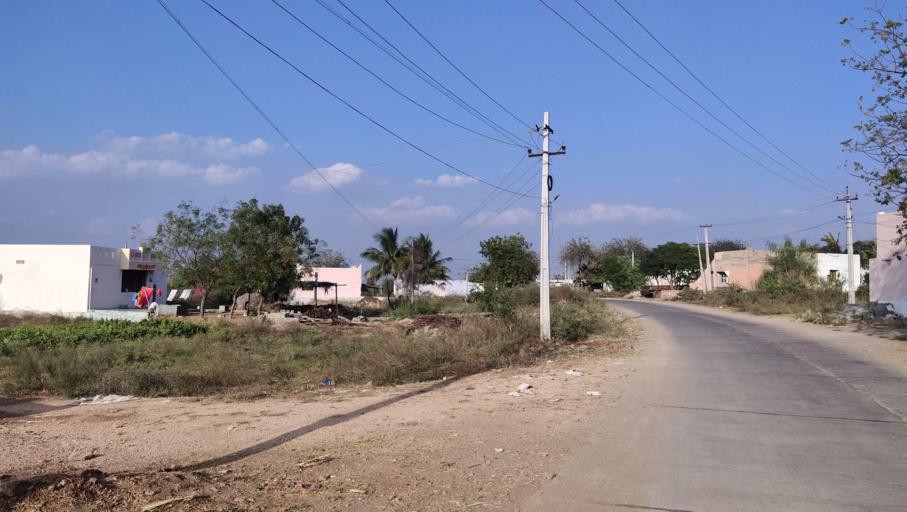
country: IN
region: Andhra Pradesh
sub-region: Anantapur
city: Tadpatri
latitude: 14.9408
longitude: 77.8696
